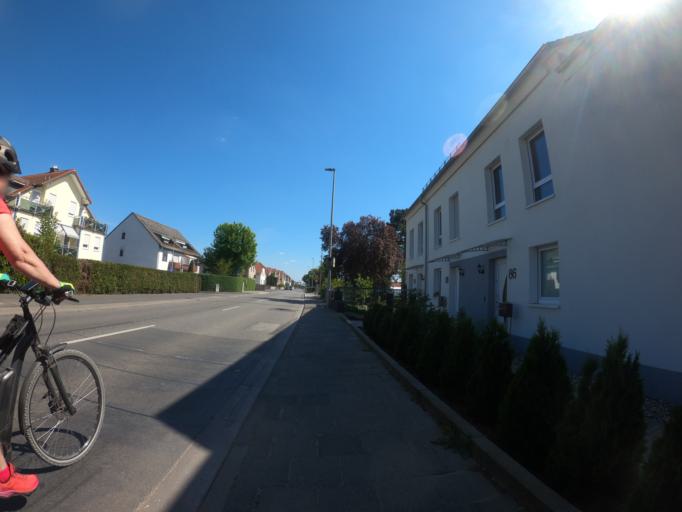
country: DE
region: Hesse
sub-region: Regierungsbezirk Darmstadt
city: Florsheim
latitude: 50.0204
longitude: 8.4187
